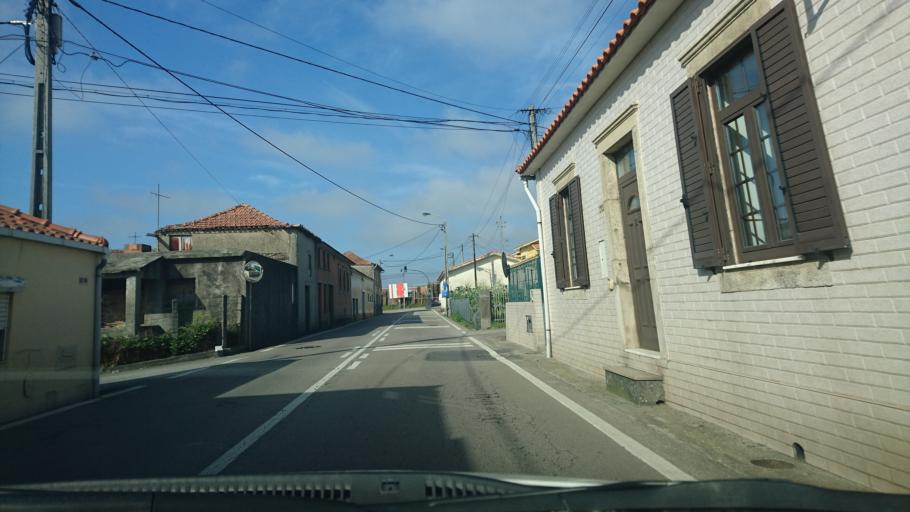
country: PT
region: Aveiro
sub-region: Ovar
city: Esmoriz
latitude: 40.9688
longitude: -8.6291
